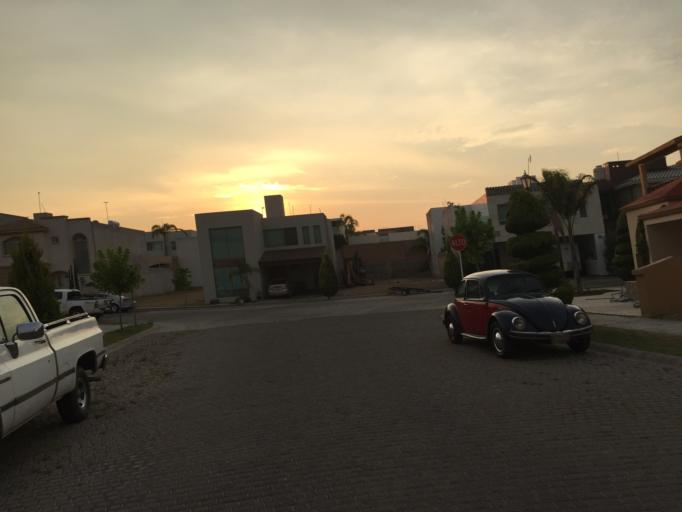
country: MX
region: Aguascalientes
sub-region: Aguascalientes
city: La Loma de los Negritos
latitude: 21.8477
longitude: -102.3557
